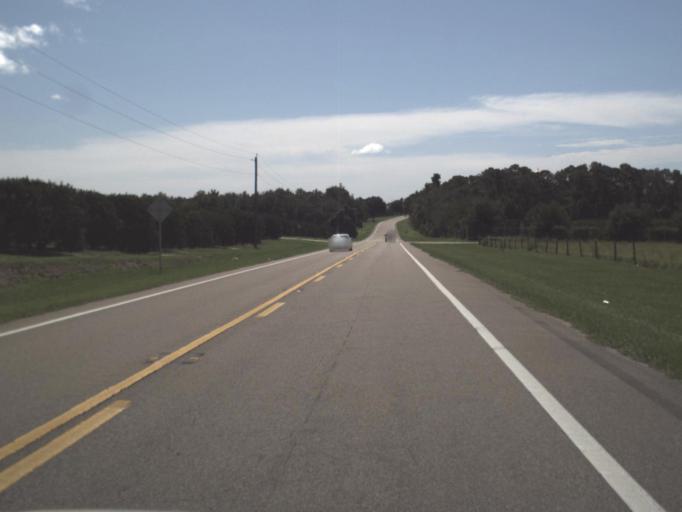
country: US
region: Florida
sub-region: Polk County
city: Polk City
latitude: 28.1772
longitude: -81.8148
